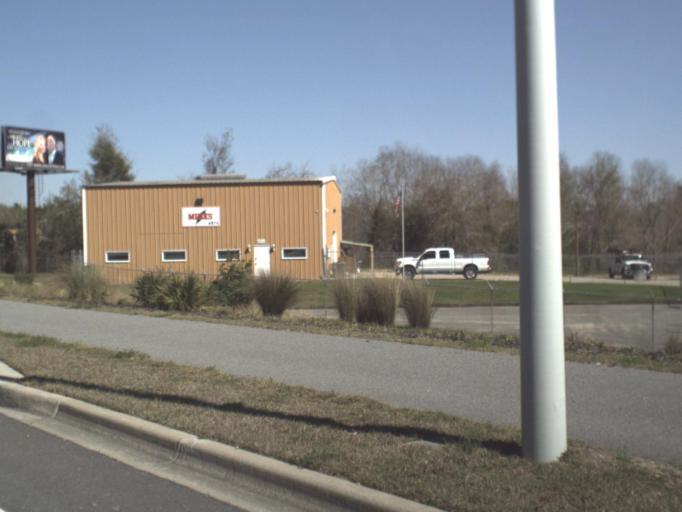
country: US
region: Florida
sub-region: Leon County
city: Woodville
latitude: 30.3767
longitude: -84.2393
